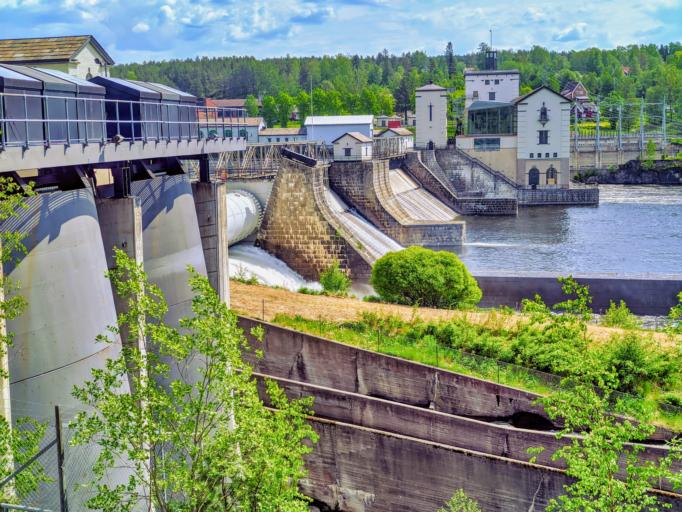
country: NO
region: Akershus
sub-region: Nes
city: Auli
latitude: 60.0287
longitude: 11.3187
